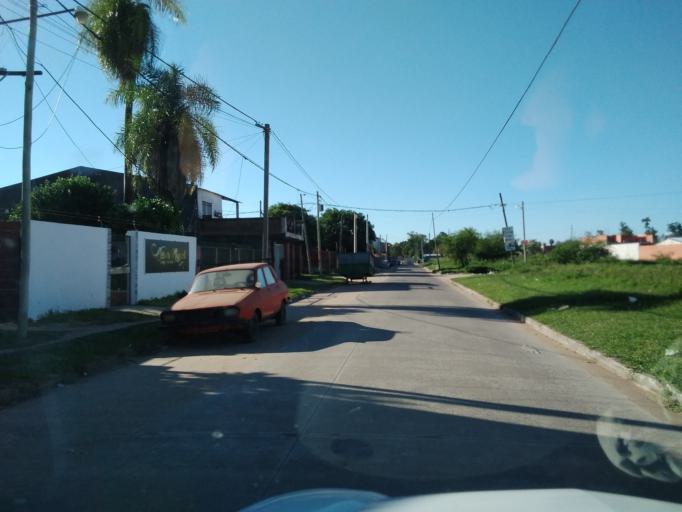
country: AR
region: Corrientes
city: Corrientes
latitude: -27.4727
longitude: -58.7964
